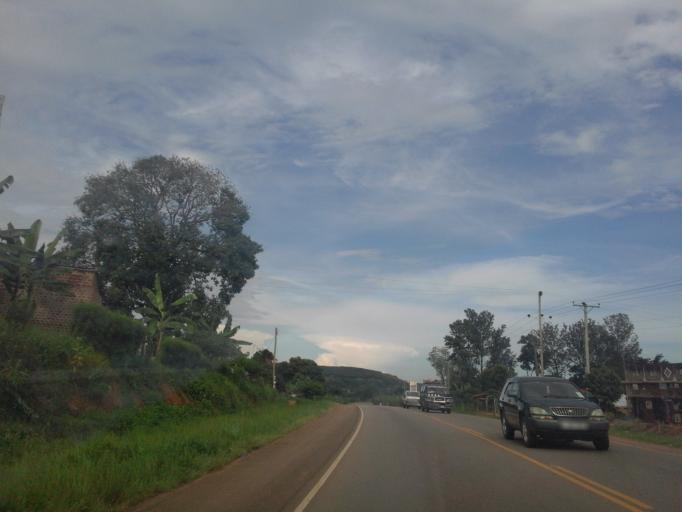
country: UG
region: Central Region
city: Masaka
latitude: -0.3451
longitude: 31.6254
